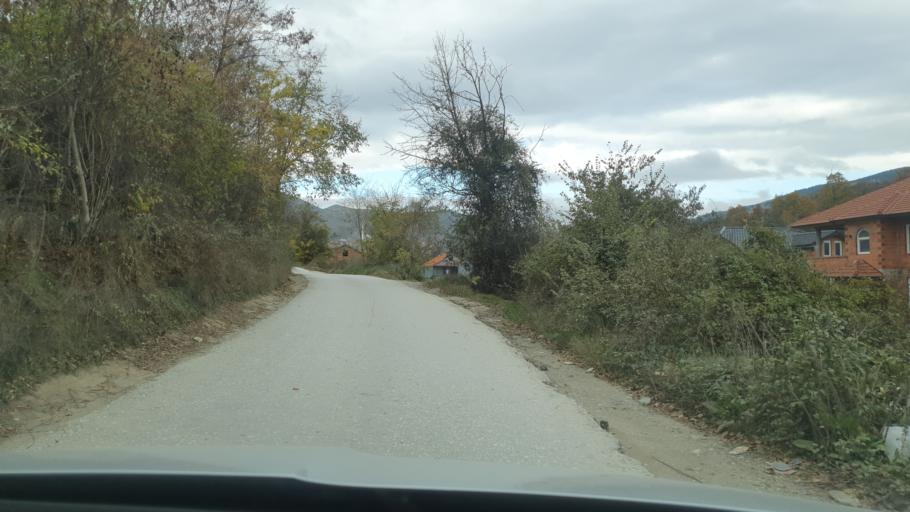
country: MK
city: Kondovo
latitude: 42.0345
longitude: 21.2828
